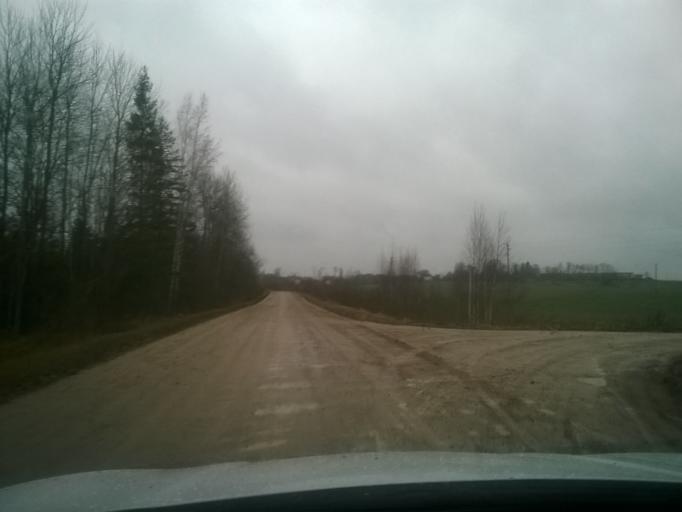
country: LV
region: Kandava
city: Kandava
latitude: 56.9510
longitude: 22.9029
